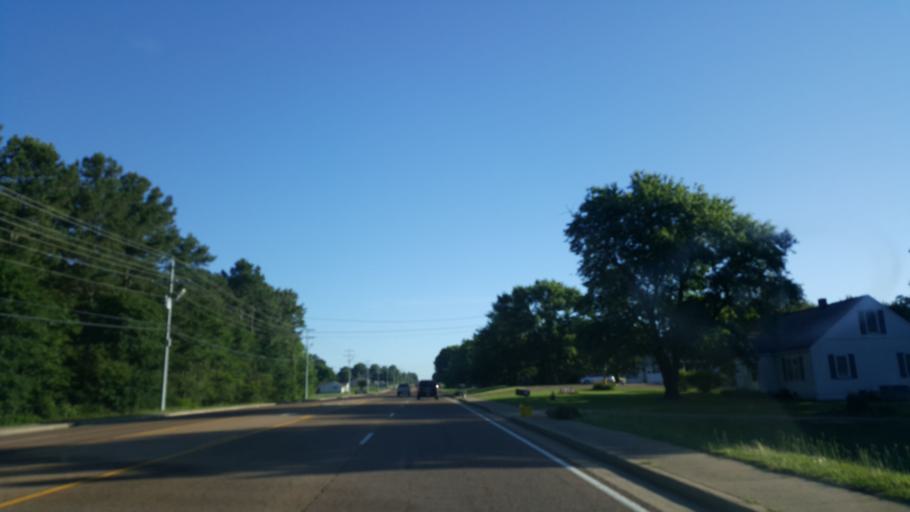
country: US
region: Tennessee
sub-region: Henderson County
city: Lexington
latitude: 35.6748
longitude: -88.3849
